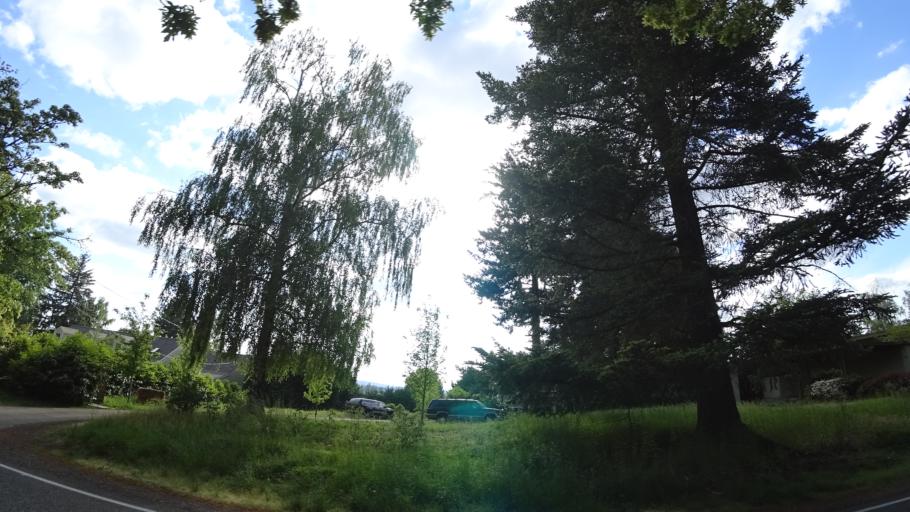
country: US
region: Oregon
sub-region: Washington County
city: Raleigh Hills
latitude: 45.4824
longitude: -122.7232
